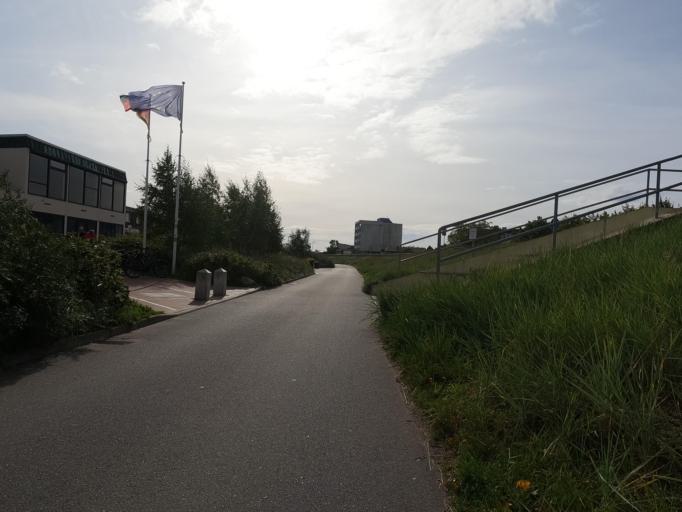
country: DE
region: Schleswig-Holstein
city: Dahme
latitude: 54.2223
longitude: 11.0879
